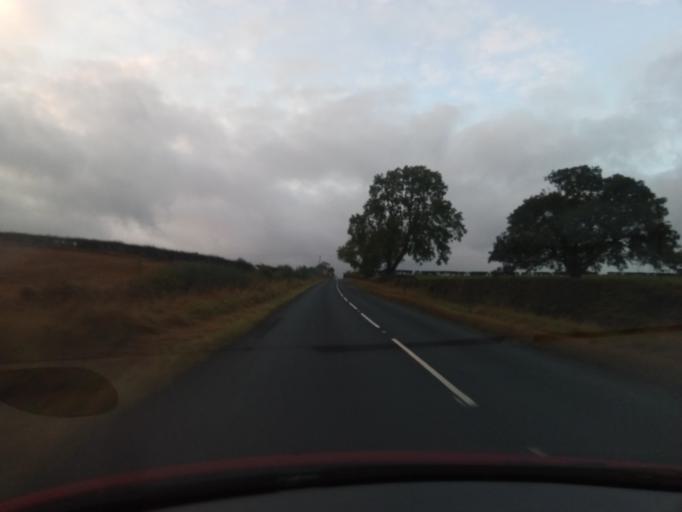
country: GB
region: England
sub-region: Darlington
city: Summerhouse
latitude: 54.5946
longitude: -1.6807
